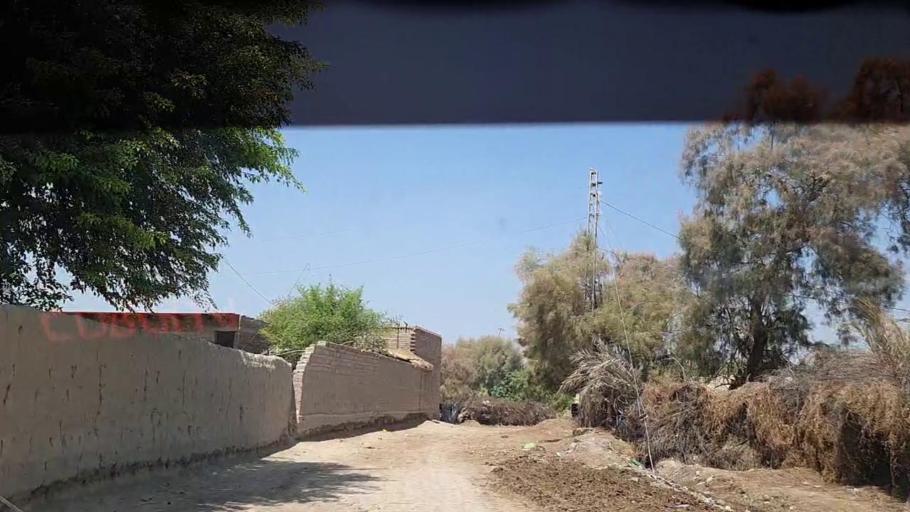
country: PK
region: Sindh
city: Ghauspur
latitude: 28.1637
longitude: 69.1432
